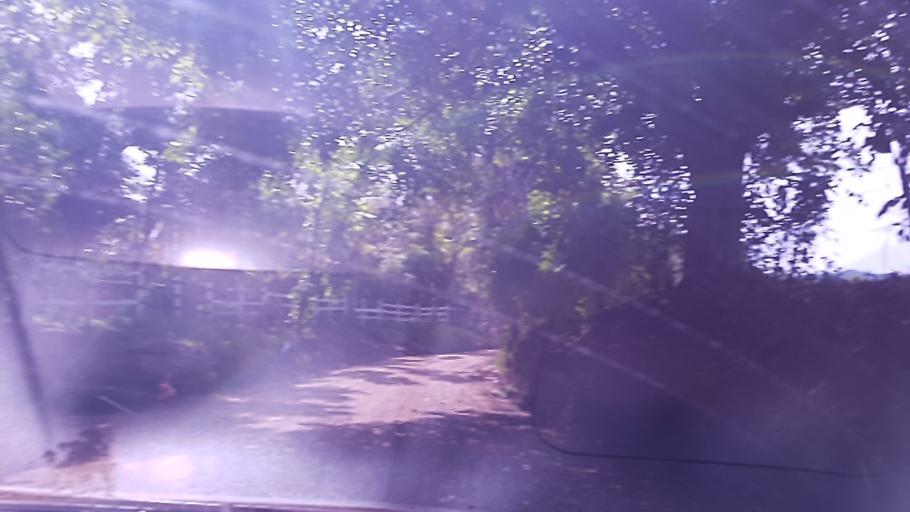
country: NI
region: Masaya
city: Ticuantepe
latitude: 11.9960
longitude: -86.2241
